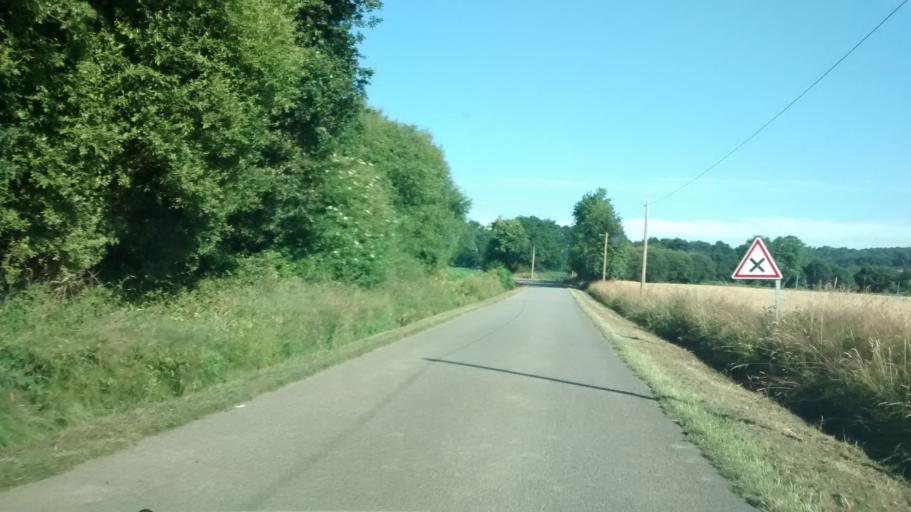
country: FR
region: Brittany
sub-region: Departement du Morbihan
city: Malestroit
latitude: 47.7867
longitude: -2.4293
